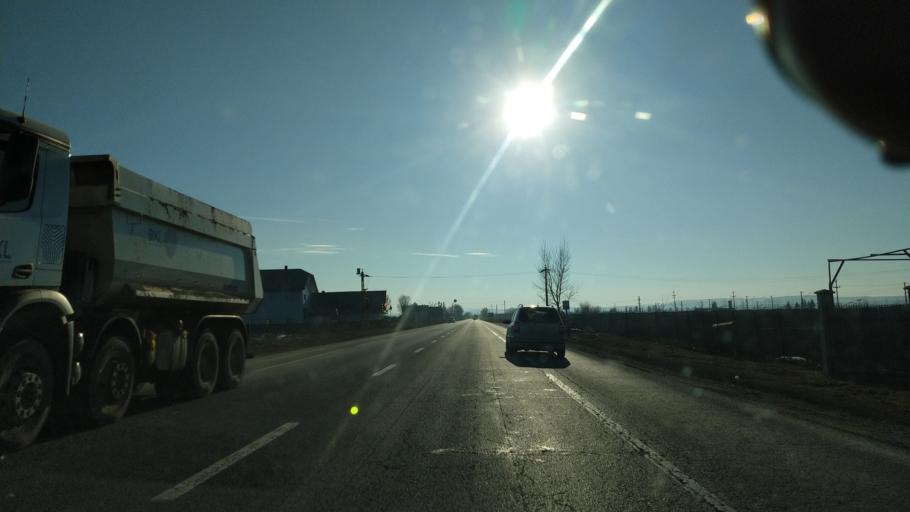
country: RO
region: Neamt
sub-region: Comuna Secueni
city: Secueni
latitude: 46.8630
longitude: 26.8910
